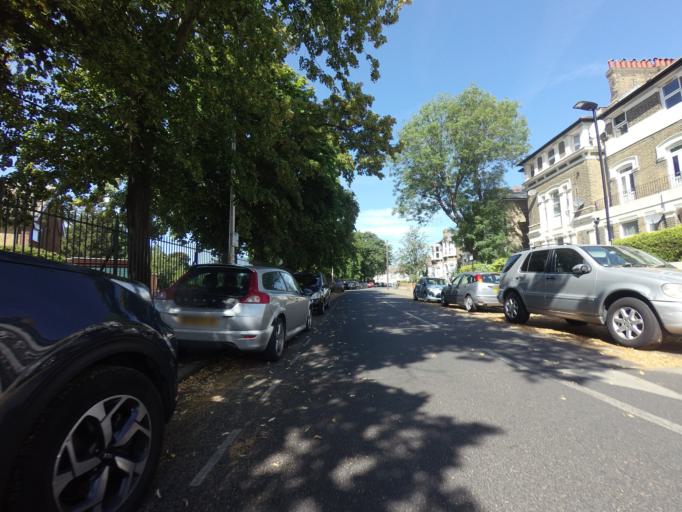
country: GB
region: England
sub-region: Greater London
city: East Ham
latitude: 51.5414
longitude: 0.0197
